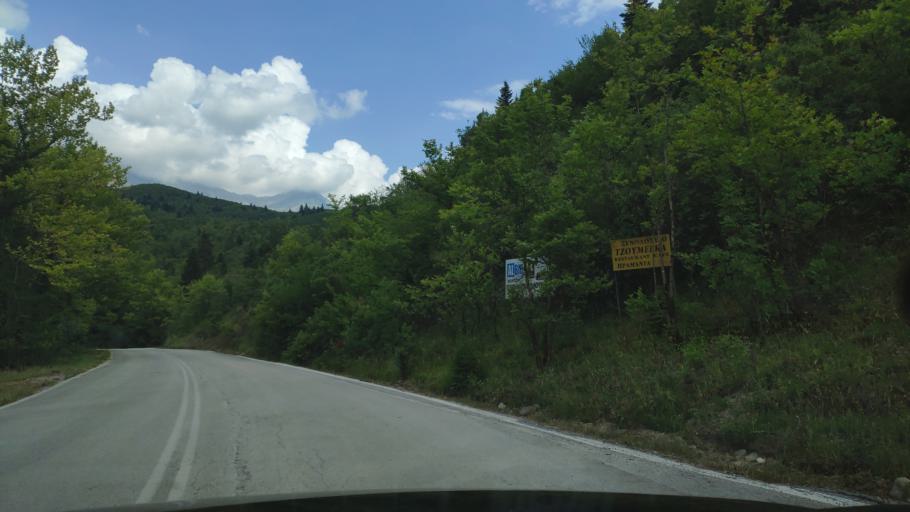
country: GR
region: Epirus
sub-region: Nomos Artas
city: Agios Dimitrios
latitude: 39.4592
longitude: 21.0632
